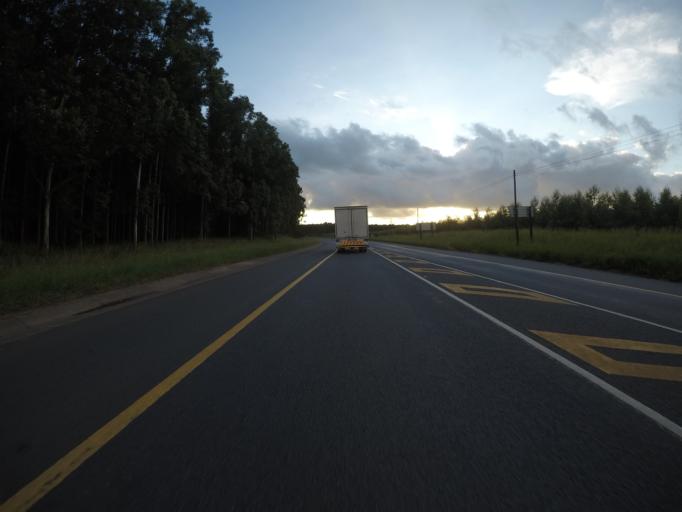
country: ZA
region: KwaZulu-Natal
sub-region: uThungulu District Municipality
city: KwaMbonambi
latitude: -28.5785
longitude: 32.1019
